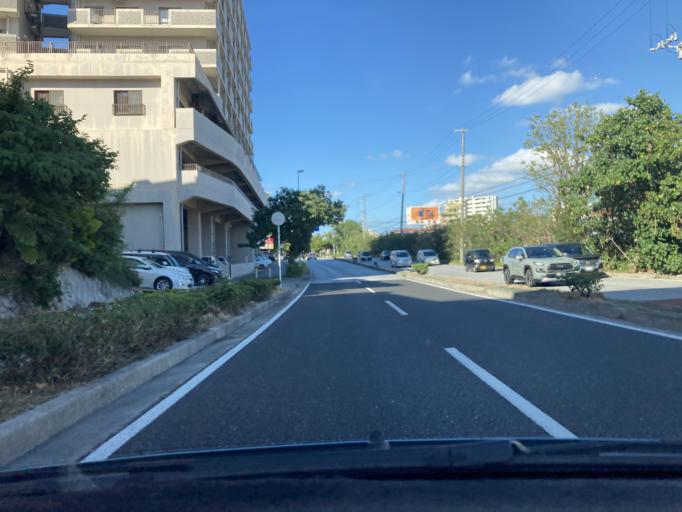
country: JP
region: Okinawa
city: Ginowan
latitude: 26.2630
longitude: 127.7261
